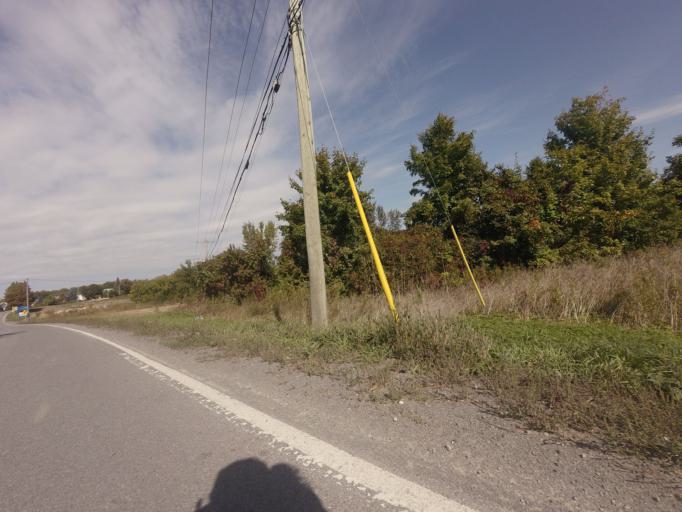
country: CA
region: Quebec
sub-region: Laurentides
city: Saint-Eustache
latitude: 45.6070
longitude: -73.9153
